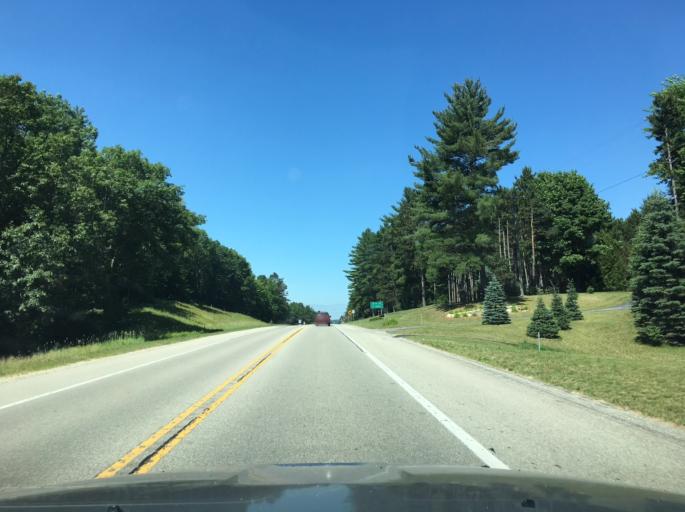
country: US
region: Michigan
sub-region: Osceola County
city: Reed City
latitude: 43.8725
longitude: -85.4403
